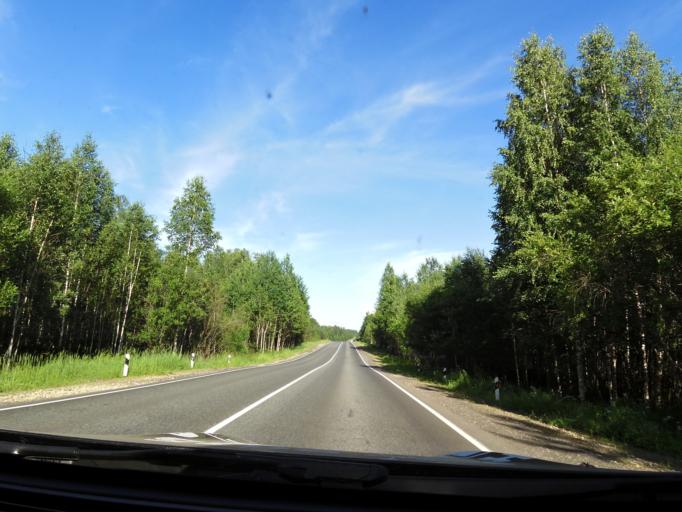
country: RU
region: Kirov
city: Chernaya Kholunitsa
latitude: 58.8731
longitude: 51.5126
